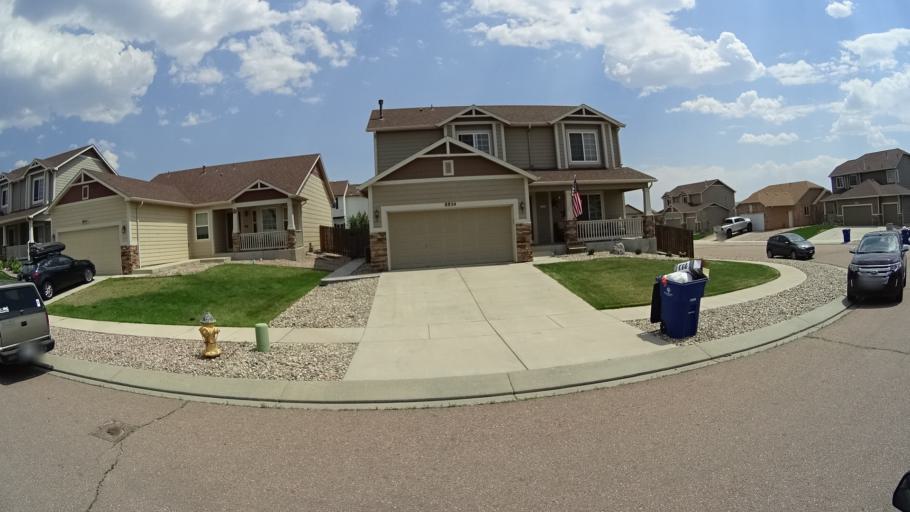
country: US
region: Colorado
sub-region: El Paso County
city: Black Forest
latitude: 38.9521
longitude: -104.7000
